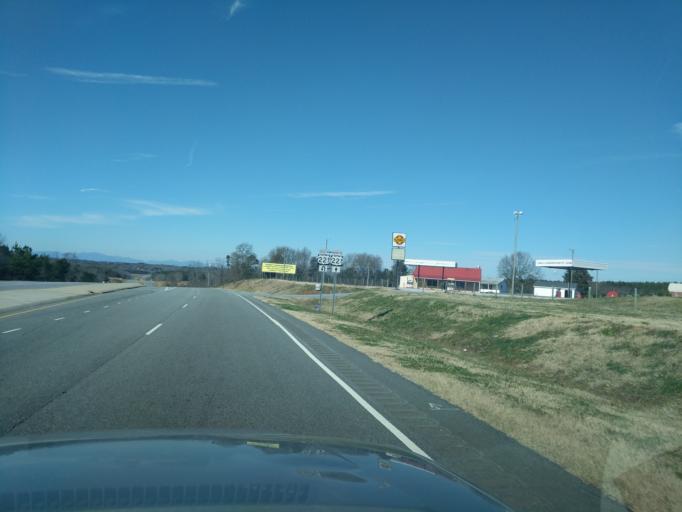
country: US
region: North Carolina
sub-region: Rutherford County
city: Forest City
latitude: 35.2367
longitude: -81.8486
